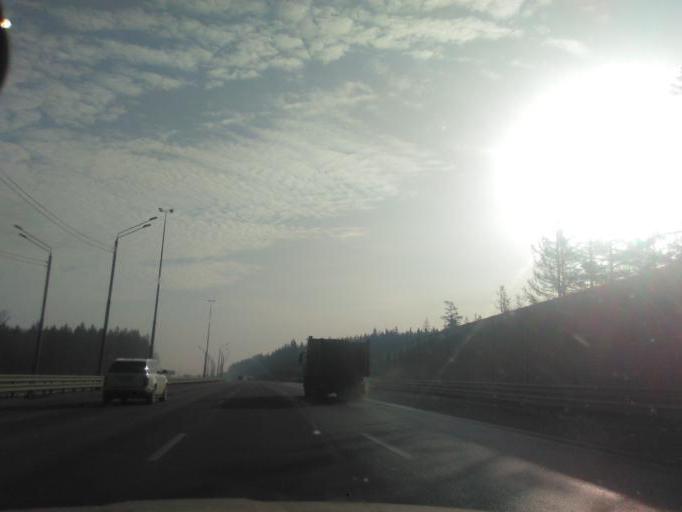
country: RU
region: Moskovskaya
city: Pavlovskaya Sloboda
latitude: 55.7848
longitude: 37.0827
